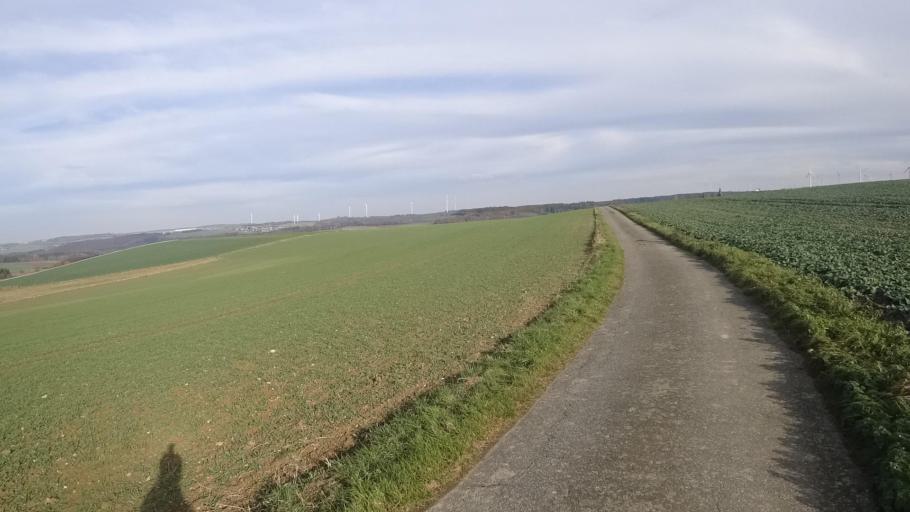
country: DE
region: Rheinland-Pfalz
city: Lingerhahn
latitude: 50.0937
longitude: 7.5535
